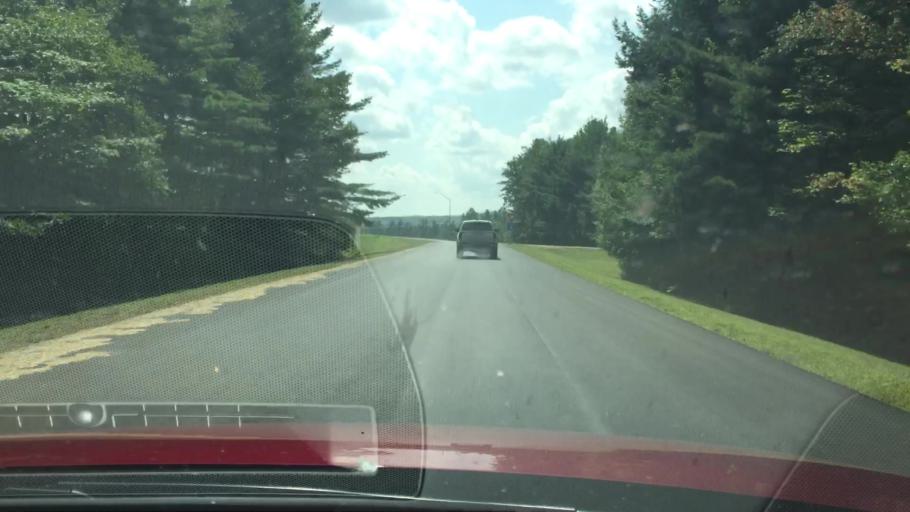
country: US
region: Maine
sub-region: Penobscot County
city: Medway
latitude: 45.5961
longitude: -68.5382
